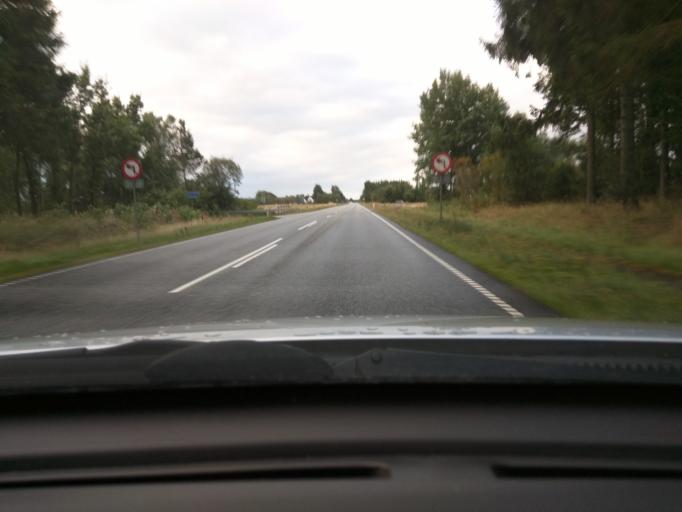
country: DK
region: Central Jutland
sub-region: Ikast-Brande Kommune
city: Bording Kirkeby
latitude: 56.2496
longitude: 9.3210
